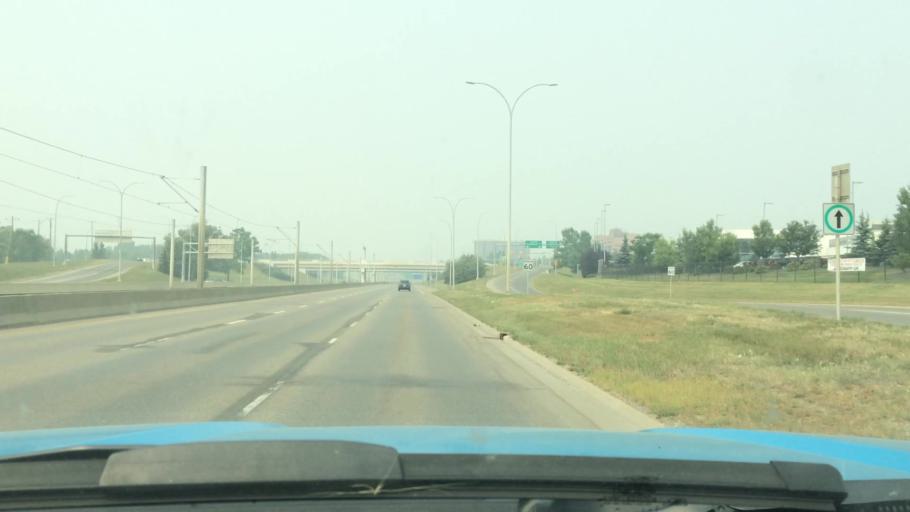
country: CA
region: Alberta
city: Calgary
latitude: 51.0956
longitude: -114.1450
